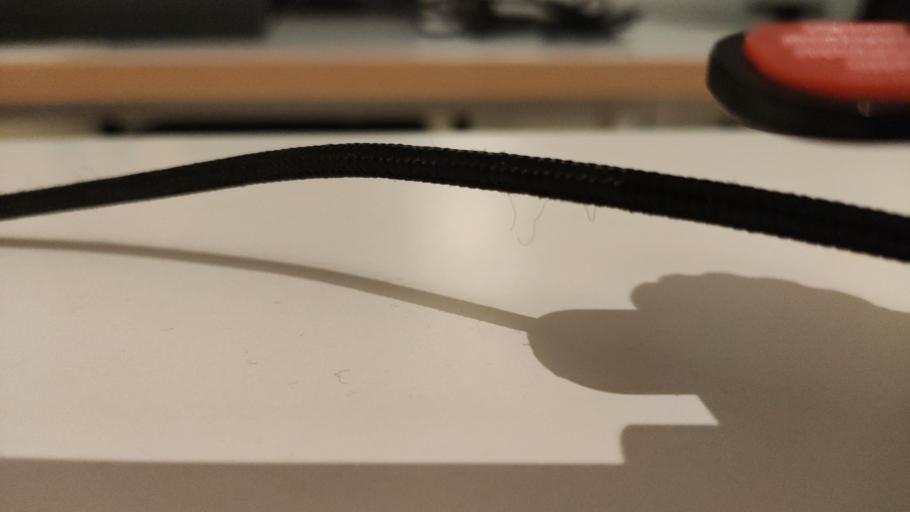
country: RU
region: Moskovskaya
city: Il'inskiy Pogost
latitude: 55.4740
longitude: 38.8646
